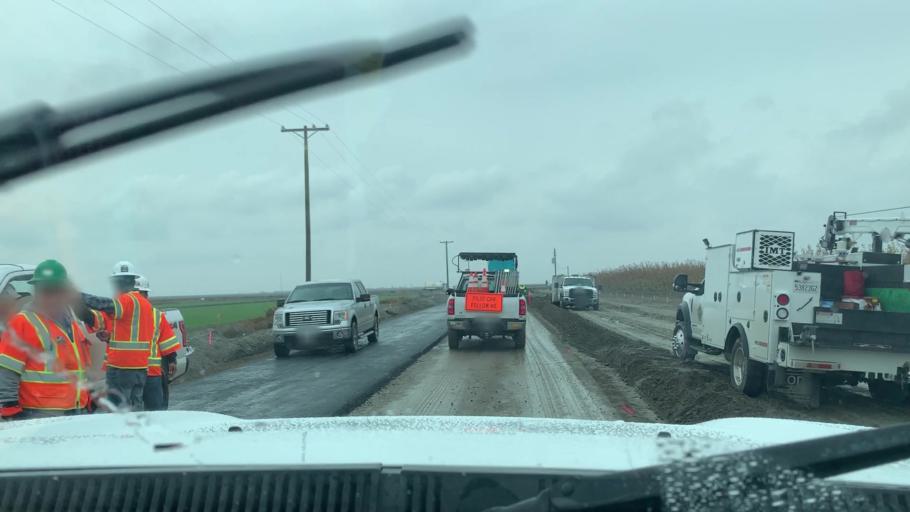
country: US
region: California
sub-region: Kings County
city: Corcoran
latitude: 36.0073
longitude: -119.5162
